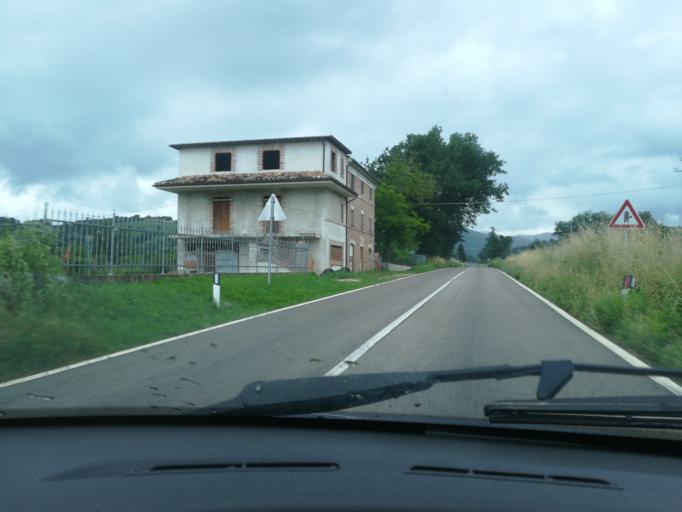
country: IT
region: The Marches
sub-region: Provincia di Macerata
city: San Ginesio
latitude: 43.0927
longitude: 13.3191
